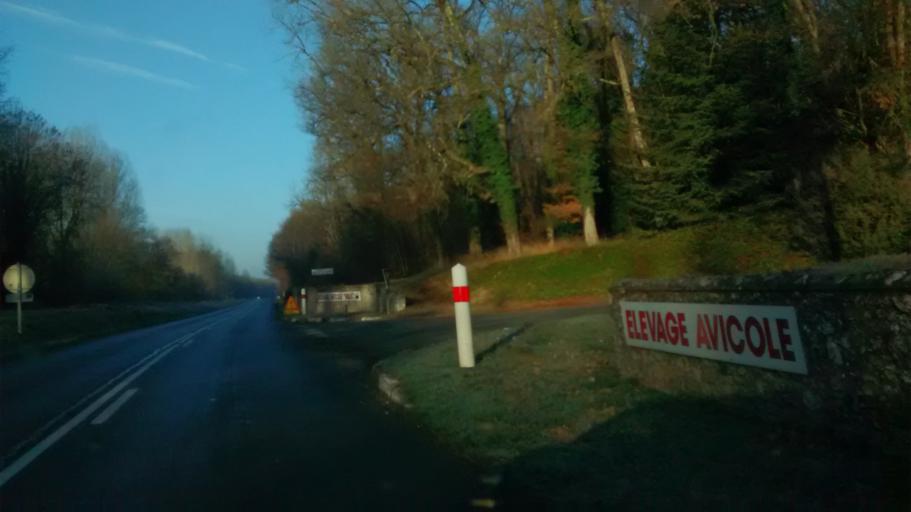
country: FR
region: Centre
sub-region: Departement d'Indre-et-Loire
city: Veigne
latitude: 47.2882
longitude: 0.7619
